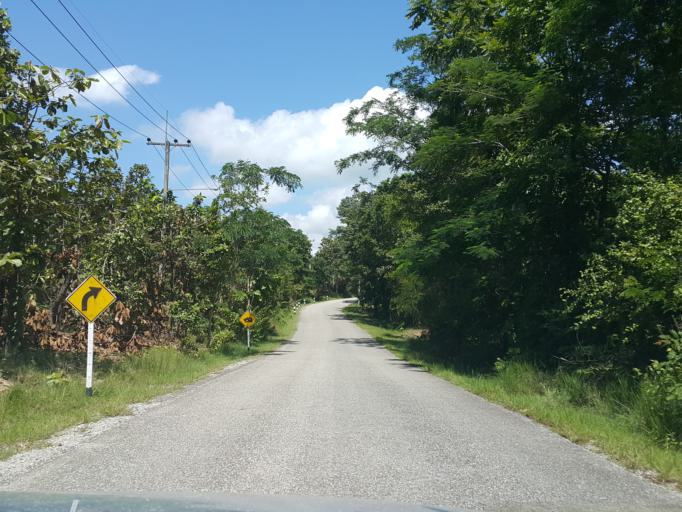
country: TH
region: Chiang Mai
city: San Kamphaeng
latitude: 18.7054
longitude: 99.1793
